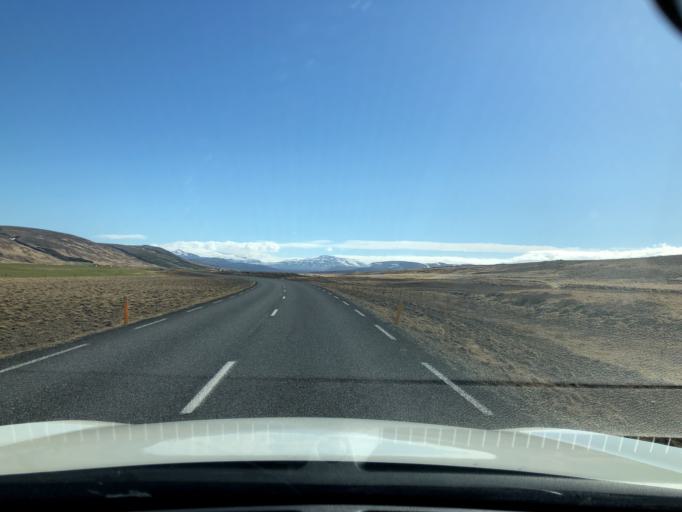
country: IS
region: South
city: Hveragerdi
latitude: 64.7013
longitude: -21.1631
